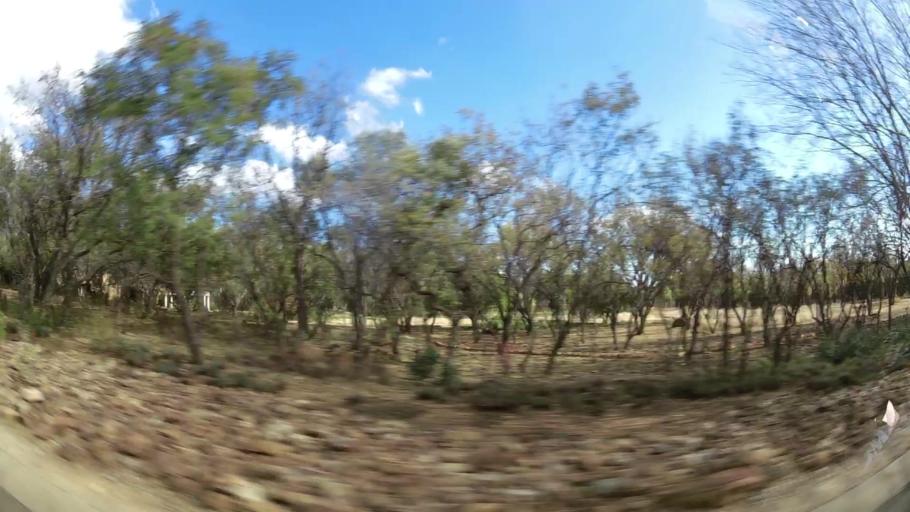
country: ZA
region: Gauteng
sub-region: West Rand District Municipality
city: Muldersdriseloop
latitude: -26.0818
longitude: 27.8557
